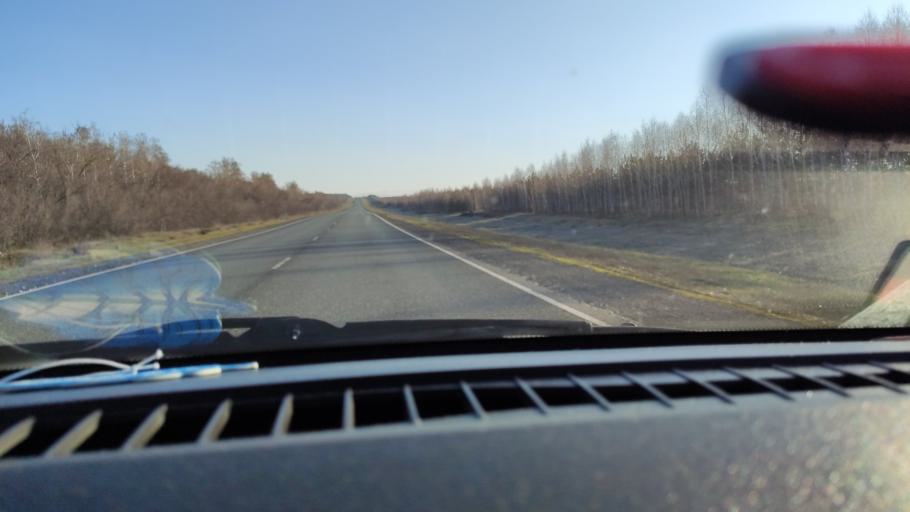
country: RU
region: Saratov
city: Balakovo
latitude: 52.1448
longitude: 47.8056
